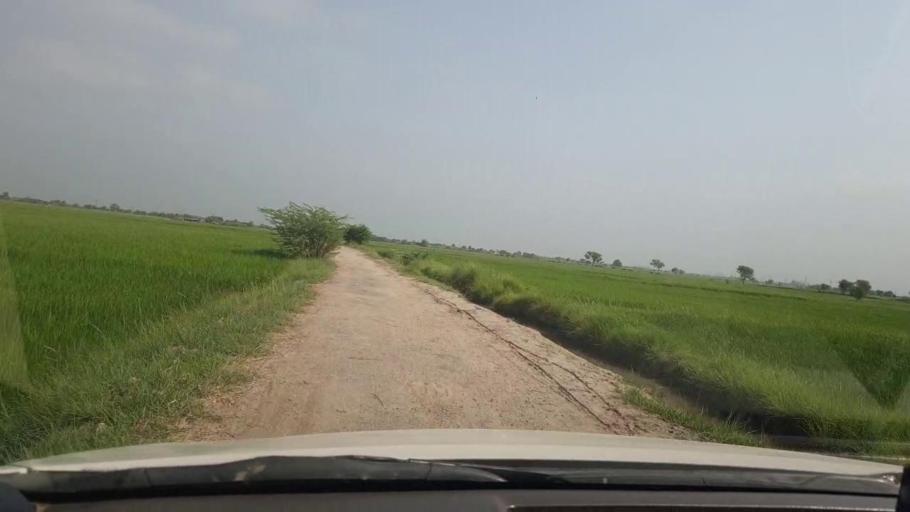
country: PK
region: Sindh
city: Shikarpur
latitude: 27.9842
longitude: 68.6094
